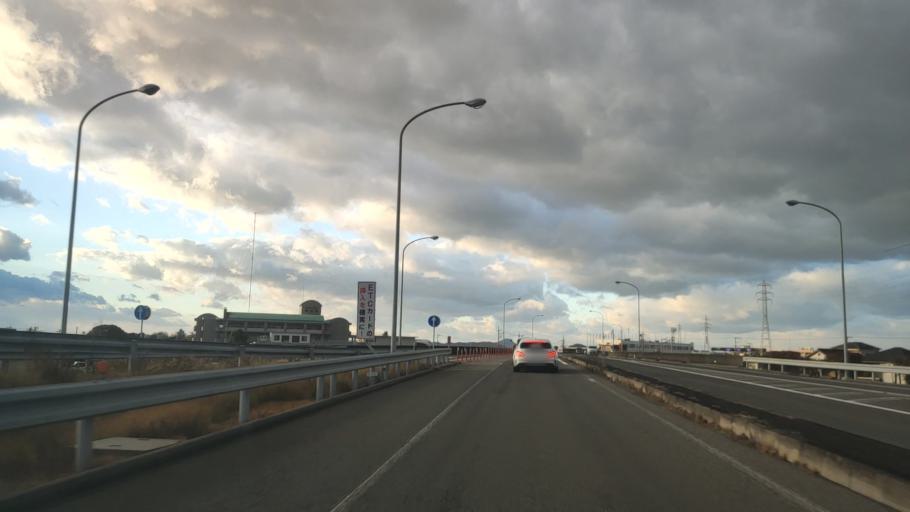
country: JP
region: Ehime
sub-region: Shikoku-chuo Shi
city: Matsuyama
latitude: 33.7956
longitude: 132.7799
